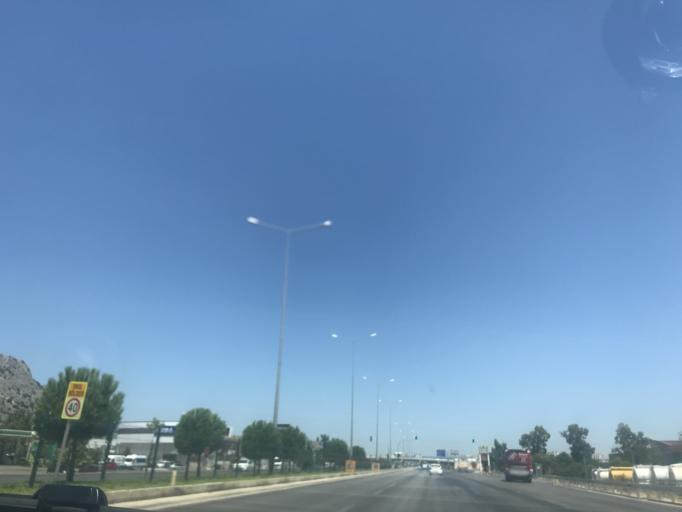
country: TR
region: Antalya
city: Cakirlar
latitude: 36.8422
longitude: 30.5980
